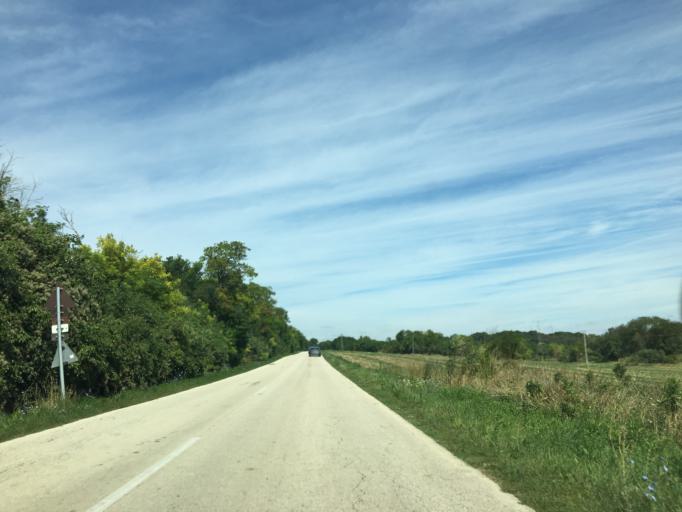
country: HU
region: Komarom-Esztergom
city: Bajna
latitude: 47.6393
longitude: 18.6089
